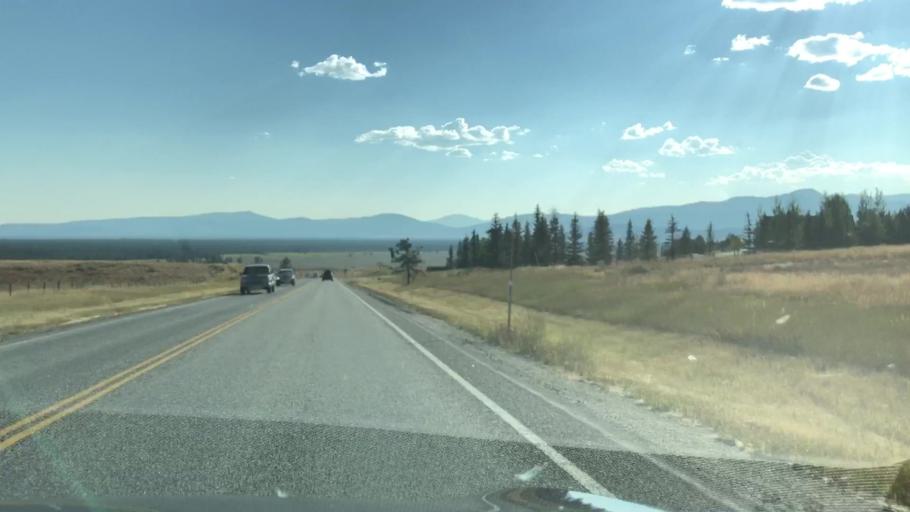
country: US
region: Montana
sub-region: Gallatin County
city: West Yellowstone
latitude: 44.7927
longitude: -111.1083
